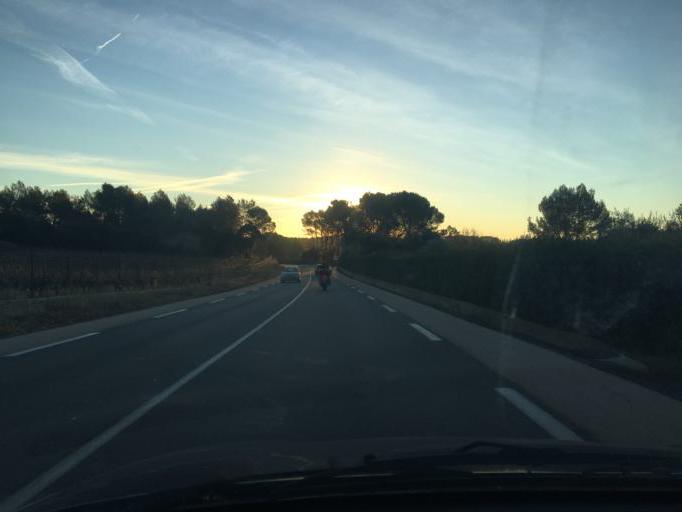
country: FR
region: Provence-Alpes-Cote d'Azur
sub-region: Departement du Var
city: Taradeau
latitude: 43.4623
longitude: 6.4026
